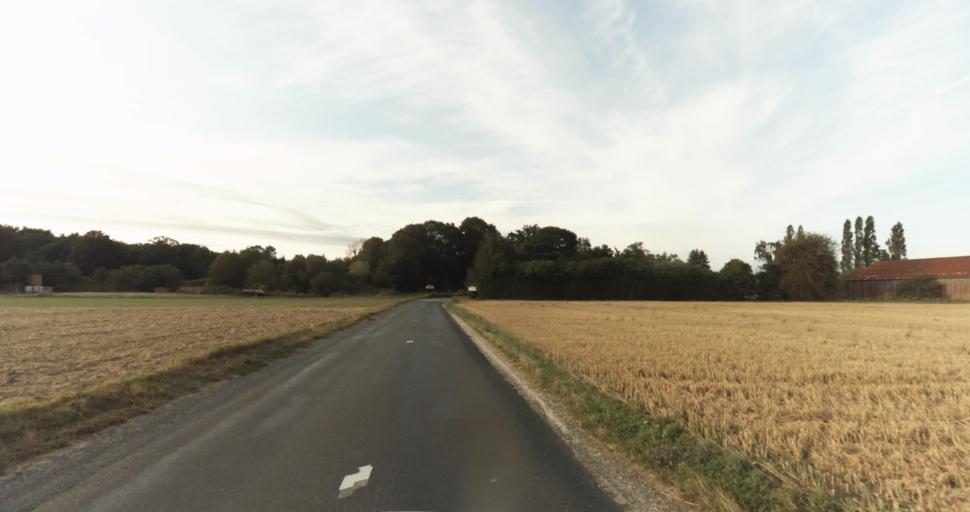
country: FR
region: Haute-Normandie
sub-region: Departement de l'Eure
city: Marcilly-sur-Eure
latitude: 48.8627
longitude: 1.2727
